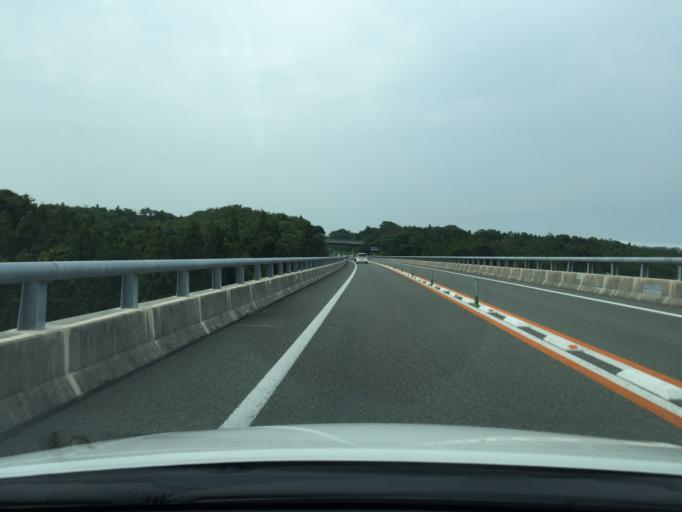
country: JP
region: Fukushima
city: Iwaki
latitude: 37.2493
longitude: 140.9897
